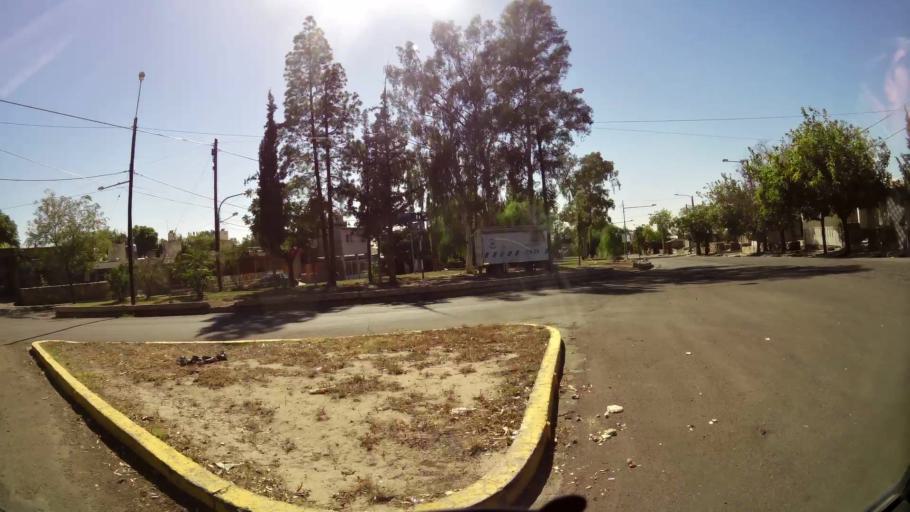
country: AR
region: Mendoza
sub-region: Departamento de Godoy Cruz
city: Godoy Cruz
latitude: -32.9042
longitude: -68.8859
